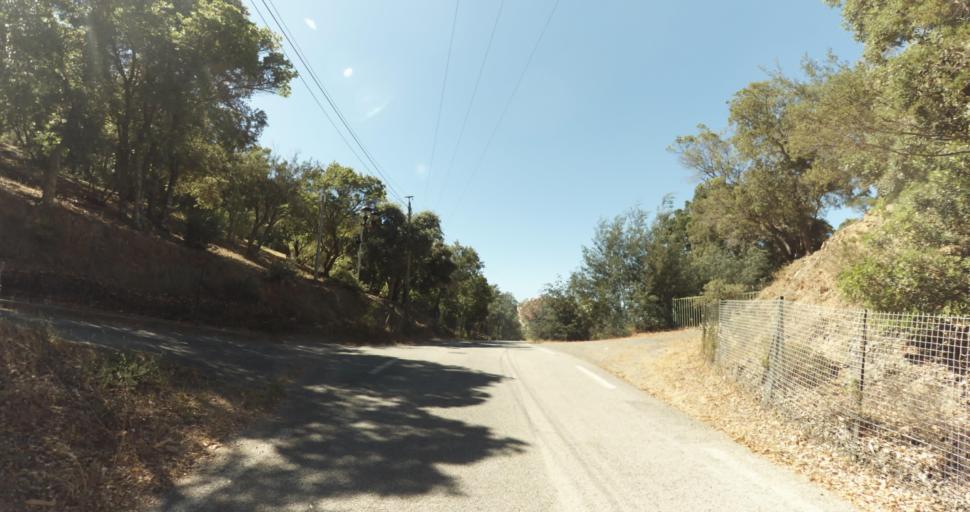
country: FR
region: Provence-Alpes-Cote d'Azur
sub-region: Departement du Var
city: La Croix-Valmer
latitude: 43.2198
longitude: 6.5551
